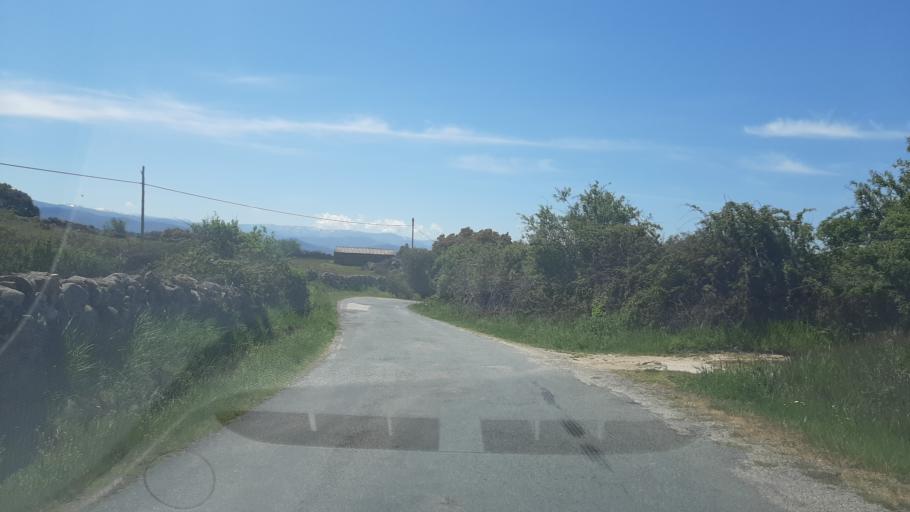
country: ES
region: Castille and Leon
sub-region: Provincia de Avila
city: Narrillos del Alamo
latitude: 40.5520
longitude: -5.4425
